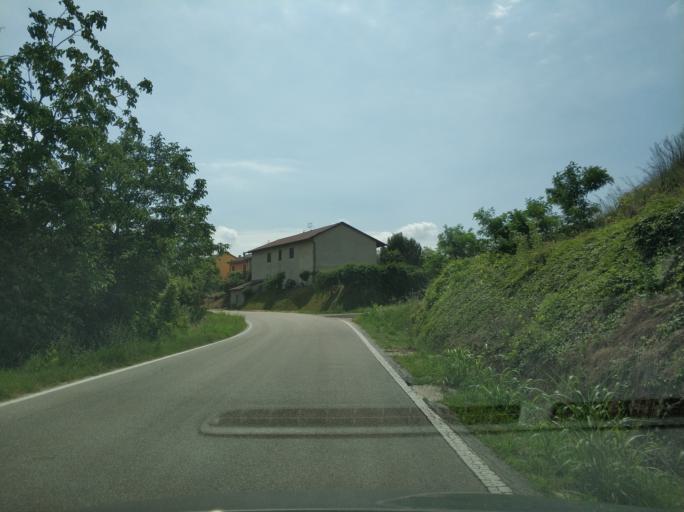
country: IT
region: Piedmont
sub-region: Provincia di Cuneo
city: Santo Stefano Roero
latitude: 44.7844
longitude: 7.9475
